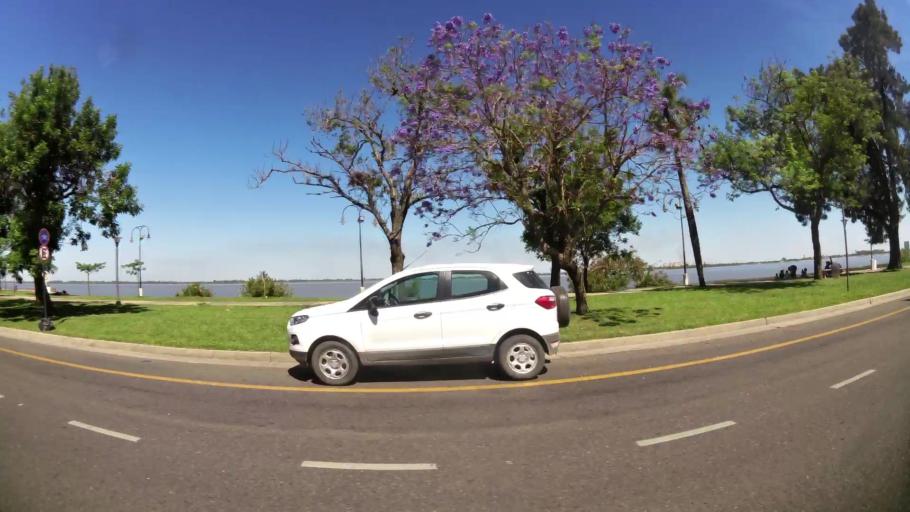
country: AR
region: Santa Fe
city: Santa Fe de la Vera Cruz
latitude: -31.6123
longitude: -60.6683
